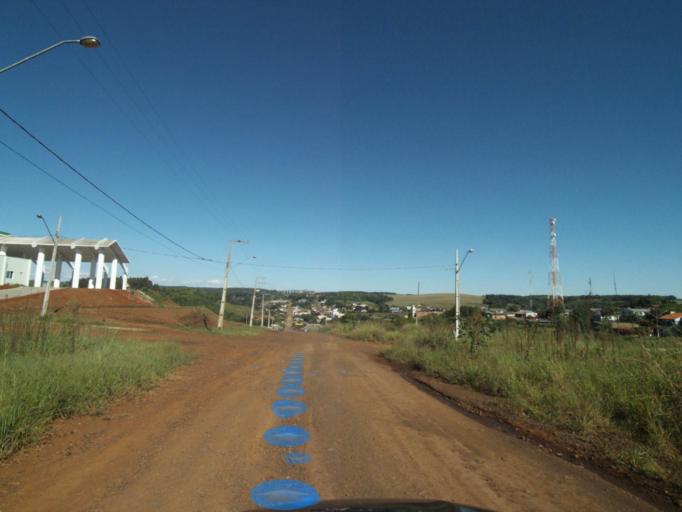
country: BR
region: Parana
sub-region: Coronel Vivida
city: Coronel Vivida
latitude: -26.1402
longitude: -52.3917
